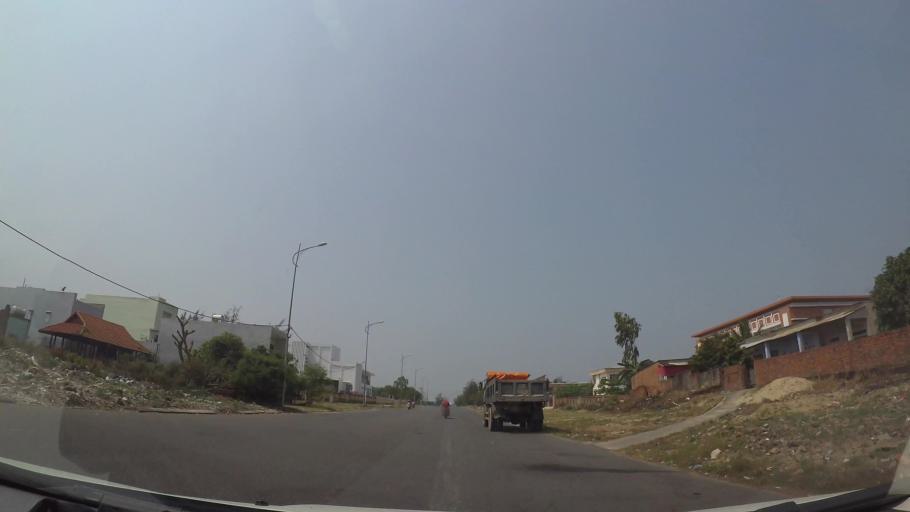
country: VN
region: Da Nang
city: Ngu Hanh Son
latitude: 16.0190
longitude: 108.2521
